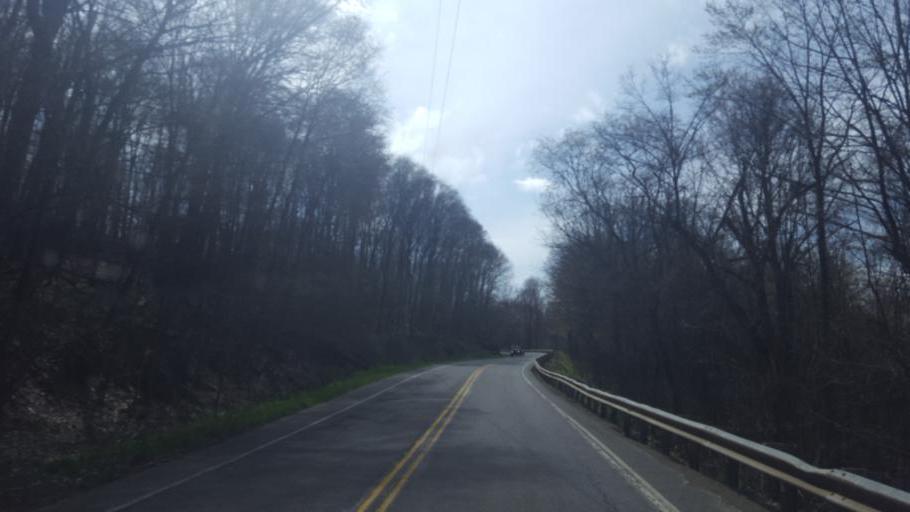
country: US
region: Pennsylvania
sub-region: Mercer County
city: Stoneboro
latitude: 41.3543
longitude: -79.9836
